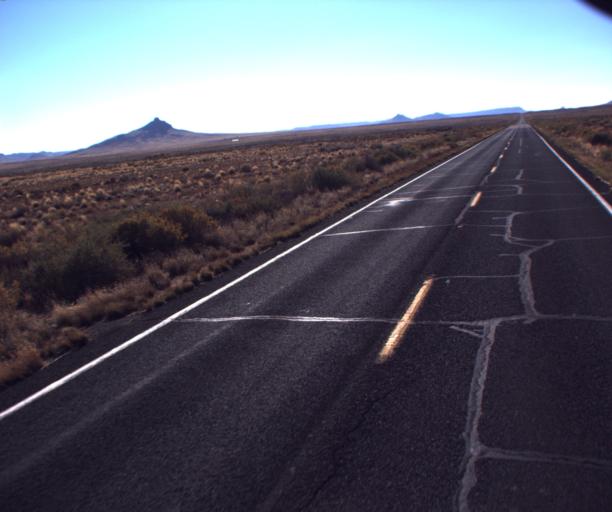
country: US
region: Arizona
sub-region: Navajo County
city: Dilkon
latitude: 35.5786
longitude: -110.4631
